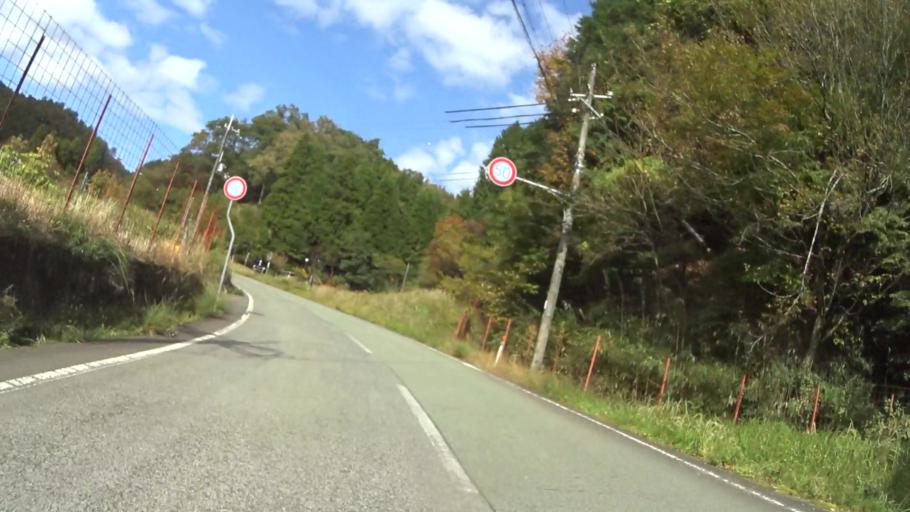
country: JP
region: Hyogo
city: Toyooka
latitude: 35.5126
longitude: 134.9916
